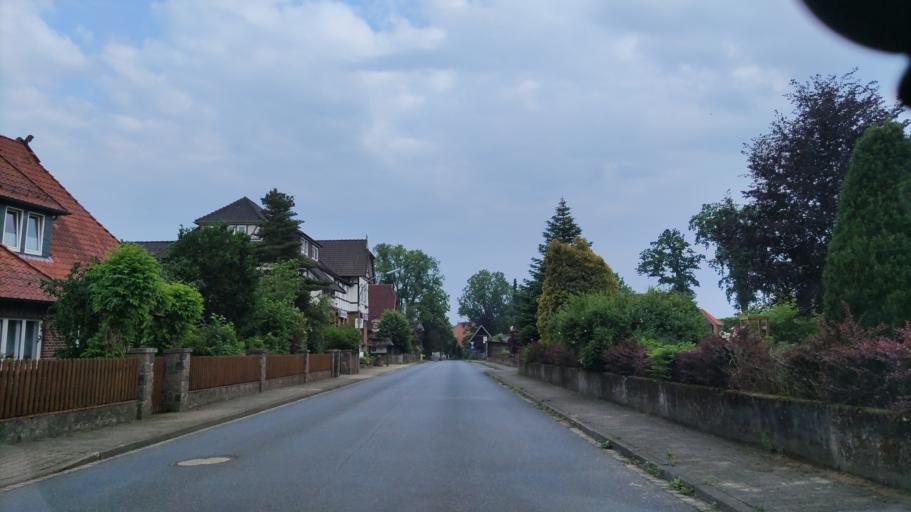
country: DE
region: Lower Saxony
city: Suderburg
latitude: 52.9306
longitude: 10.4435
